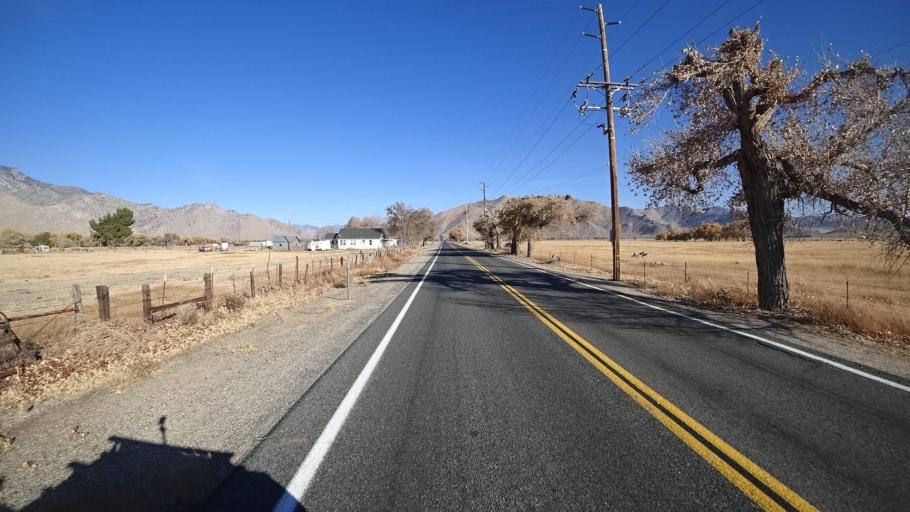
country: US
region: California
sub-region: Kern County
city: Weldon
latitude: 35.6655
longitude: -118.2935
